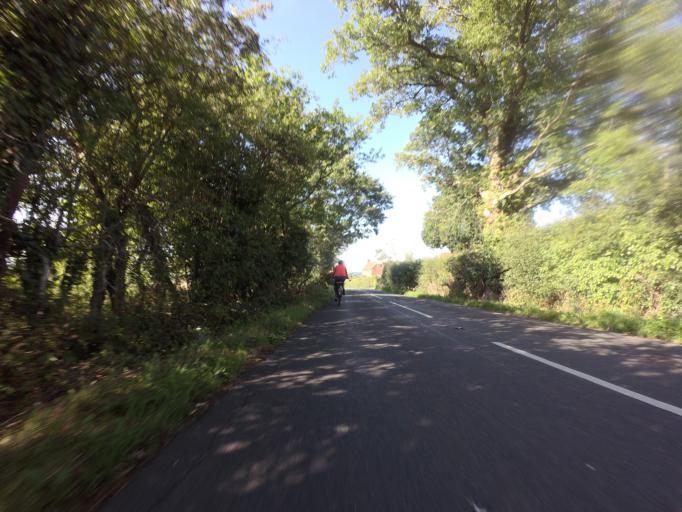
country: GB
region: England
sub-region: Kent
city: Tenterden
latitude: 51.0240
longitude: 0.6929
